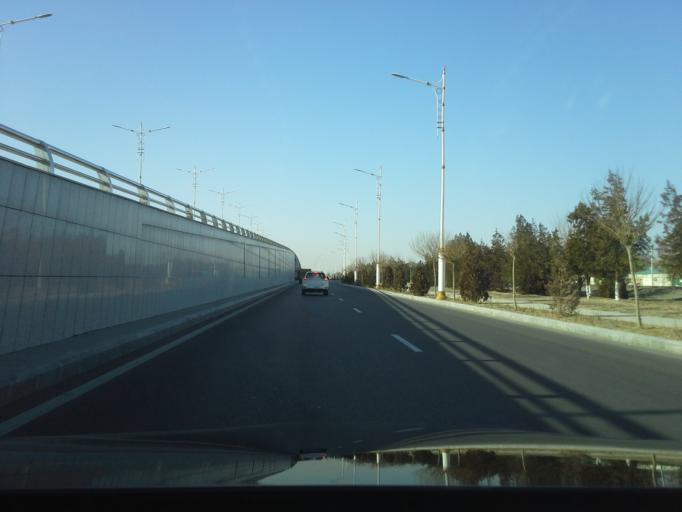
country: TM
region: Ahal
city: Ashgabat
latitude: 37.9608
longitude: 58.3647
